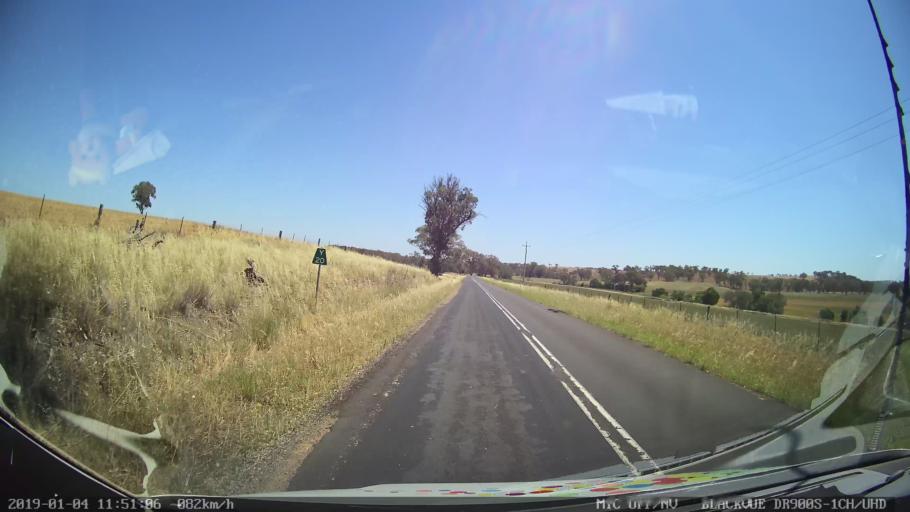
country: AU
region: New South Wales
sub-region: Cabonne
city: Molong
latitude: -32.8985
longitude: 148.7579
